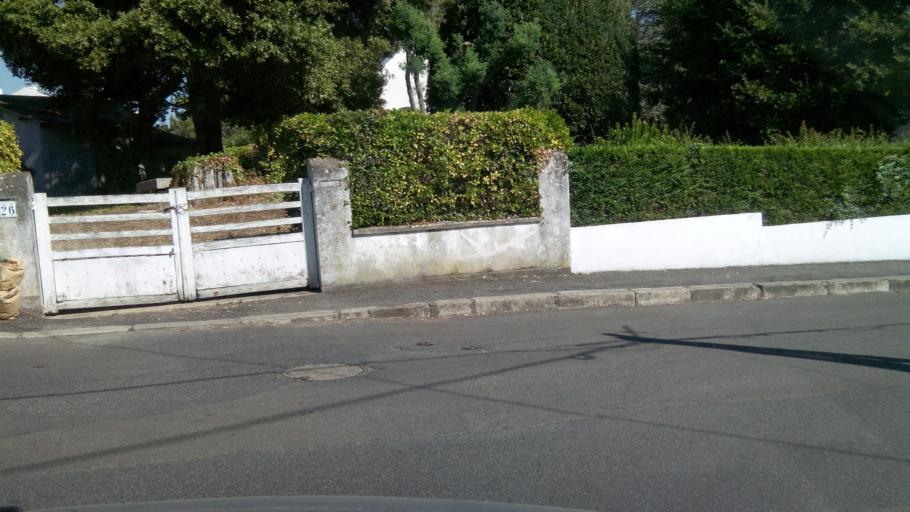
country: FR
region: Pays de la Loire
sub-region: Departement de la Loire-Atlantique
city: Pornichet
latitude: 47.2729
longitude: -2.3448
